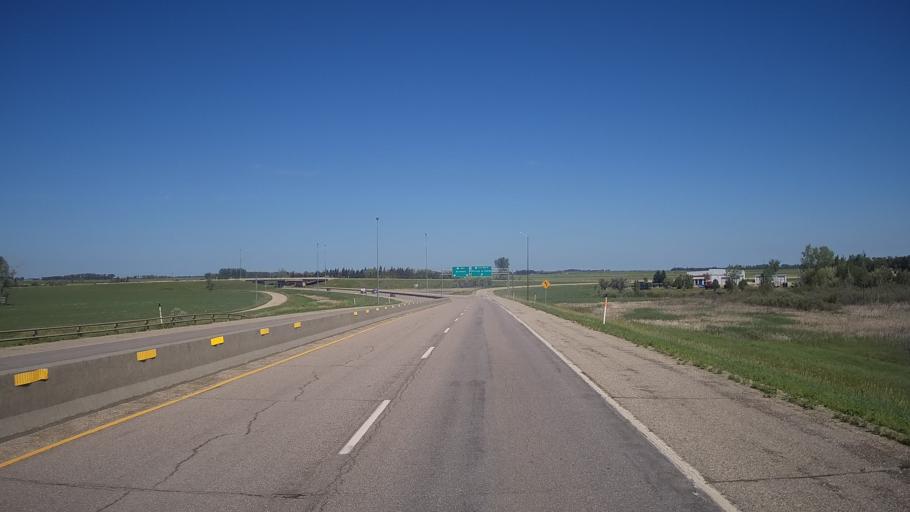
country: CA
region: Manitoba
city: Portage la Prairie
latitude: 49.9688
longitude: -98.3578
